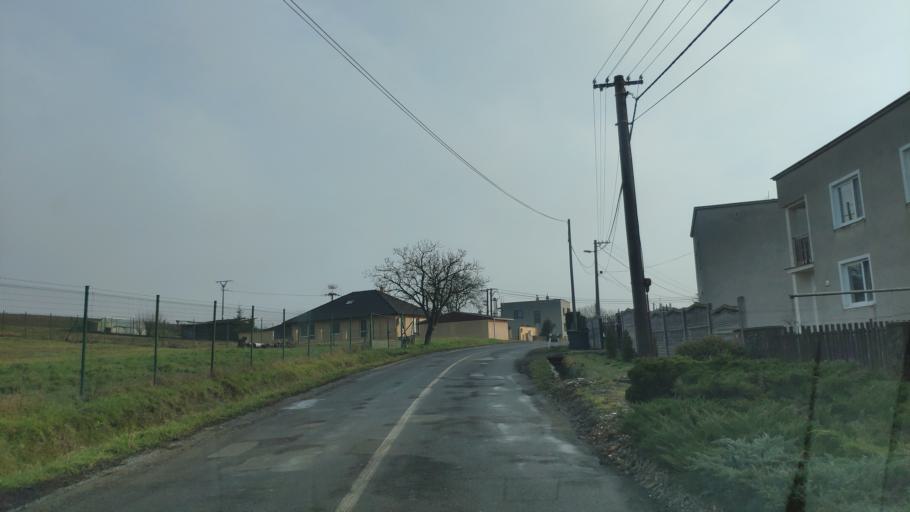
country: SK
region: Kosicky
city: Kosice
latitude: 48.7080
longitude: 21.4009
